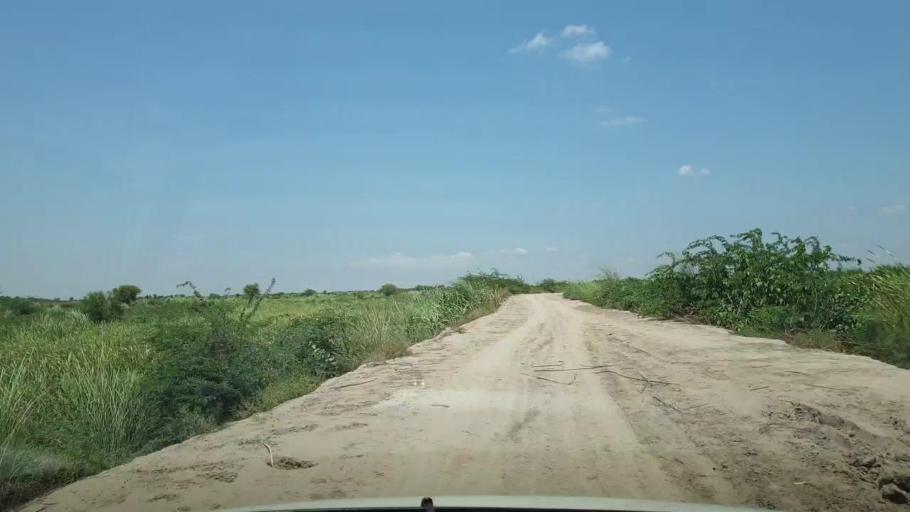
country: PK
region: Sindh
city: Sanghar
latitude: 26.1044
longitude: 69.0046
